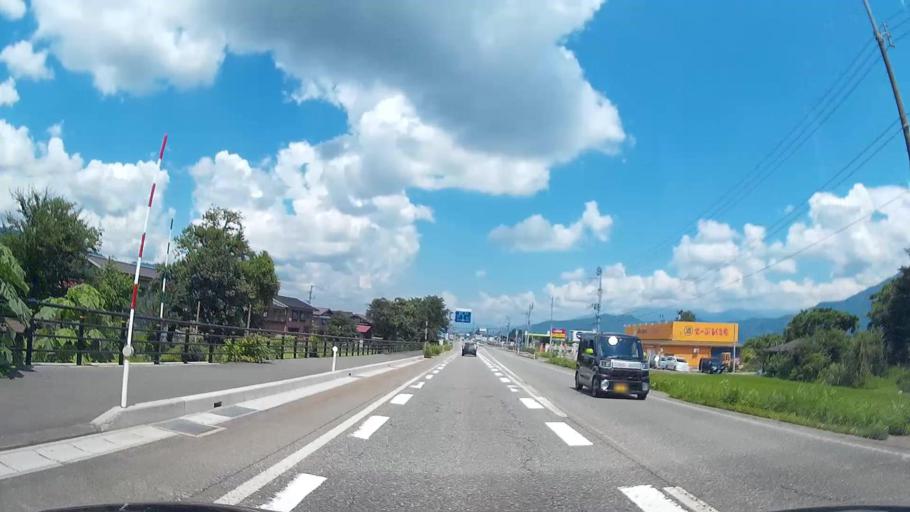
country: JP
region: Niigata
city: Shiozawa
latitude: 37.0142
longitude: 138.8269
